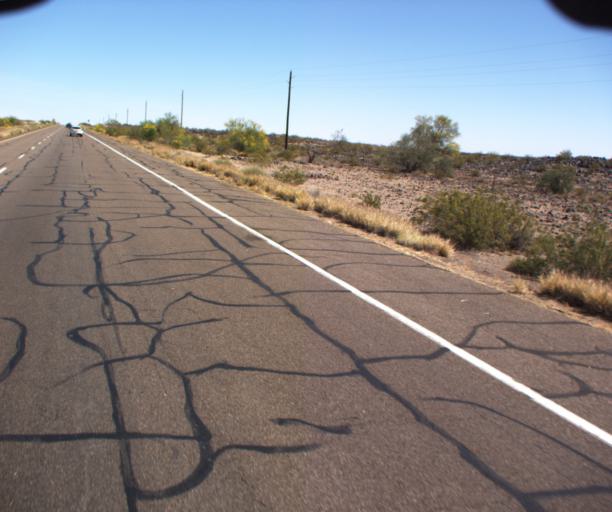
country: US
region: Arizona
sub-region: Maricopa County
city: Gila Bend
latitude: 32.8514
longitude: -113.2605
